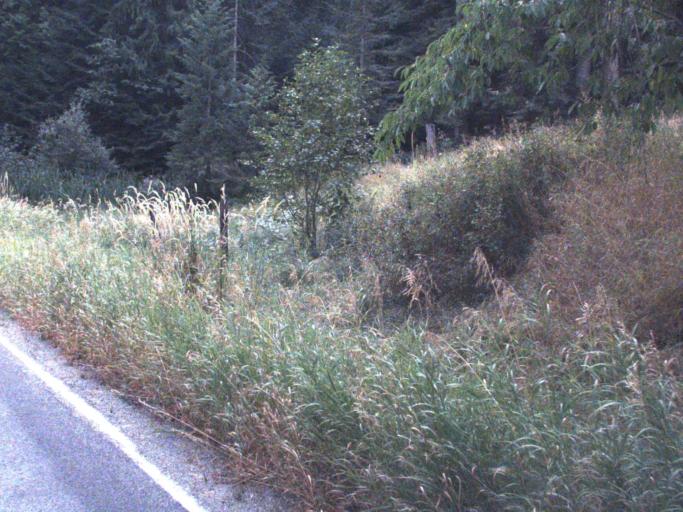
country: US
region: Washington
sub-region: Spokane County
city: Trentwood
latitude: 47.8581
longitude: -117.1631
